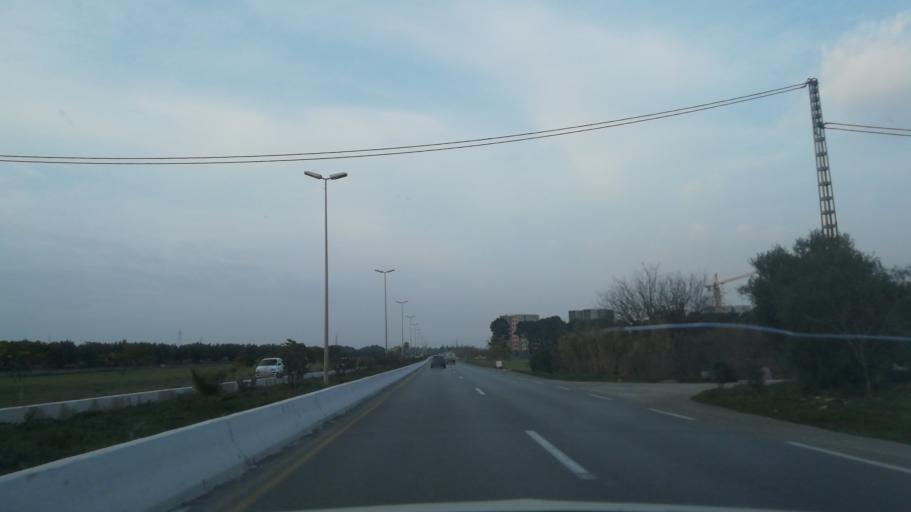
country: DZ
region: Sidi Bel Abbes
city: Sidi Bel Abbes
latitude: 35.2014
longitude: -0.6603
